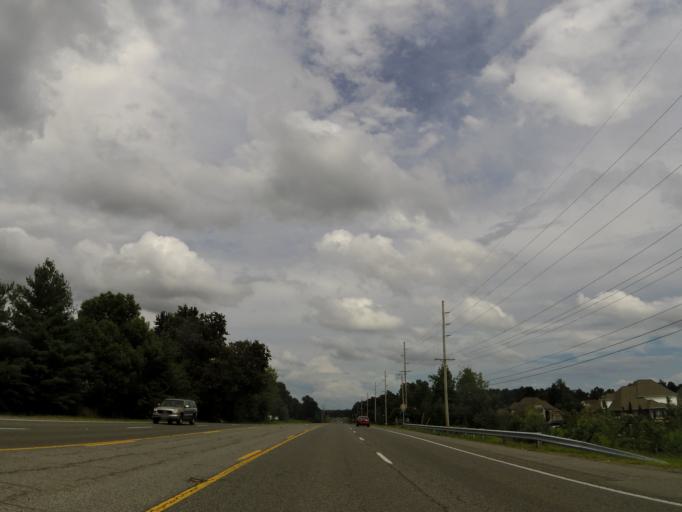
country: US
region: Kentucky
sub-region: McCracken County
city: Massac
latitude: 37.0454
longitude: -88.7039
